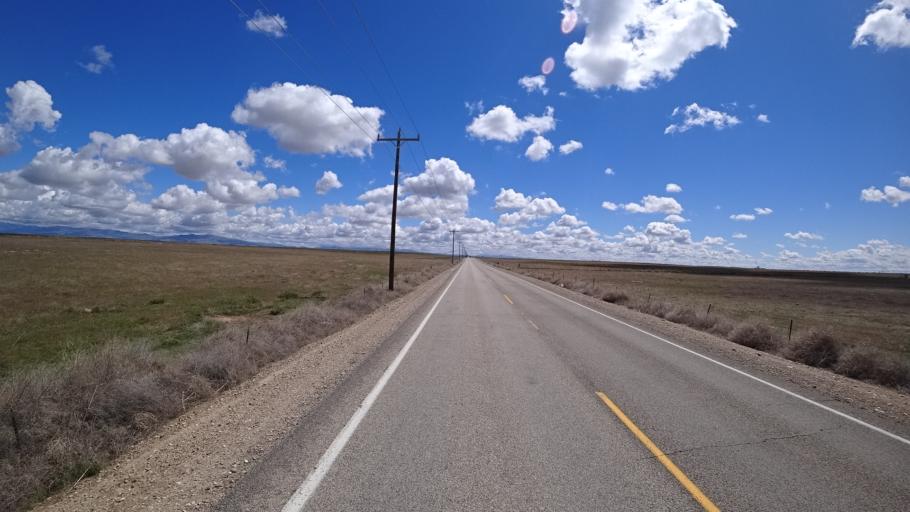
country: US
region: Idaho
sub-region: Ada County
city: Kuna
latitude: 43.4592
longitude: -116.3109
